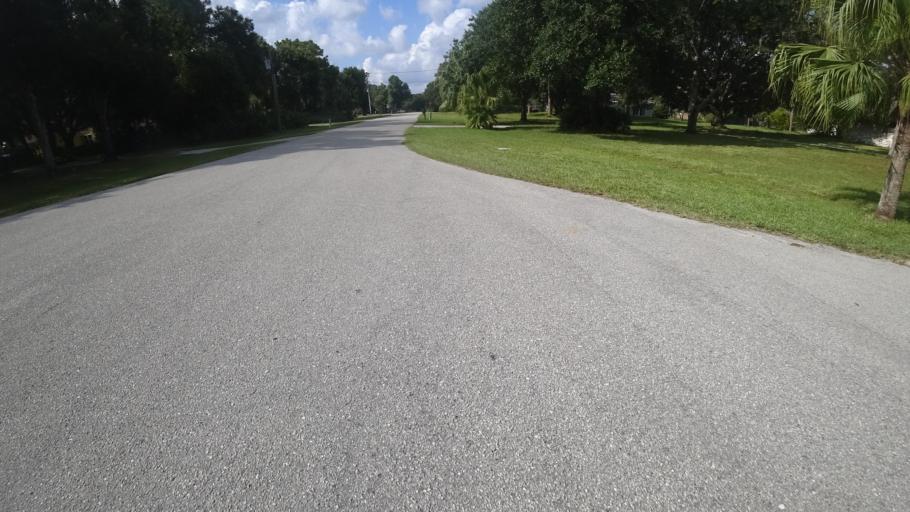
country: US
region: Florida
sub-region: Sarasota County
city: The Meadows
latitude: 27.4295
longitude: -82.4444
